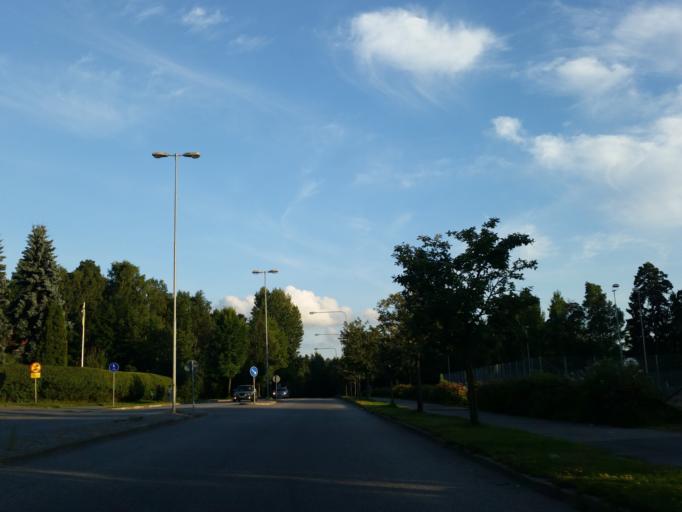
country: SE
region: Stockholm
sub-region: Sodertalje Kommun
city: Soedertaelje
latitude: 59.2056
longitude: 17.6004
